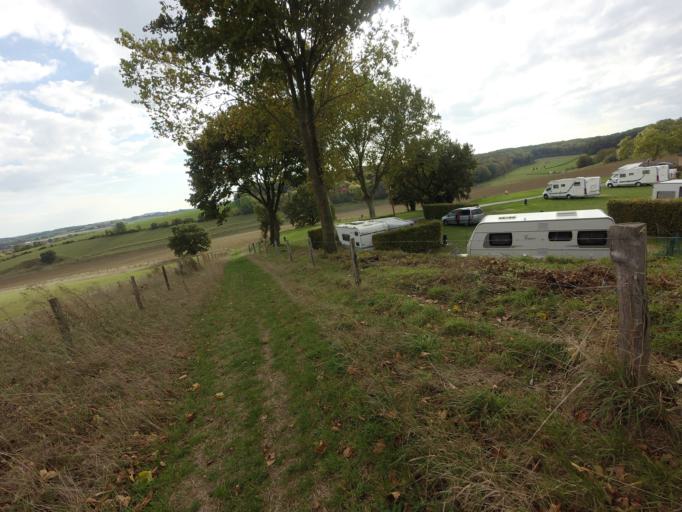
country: NL
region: Limburg
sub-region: Valkenburg aan de Geul
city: Schin op Geul
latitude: 50.8089
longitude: 5.9001
